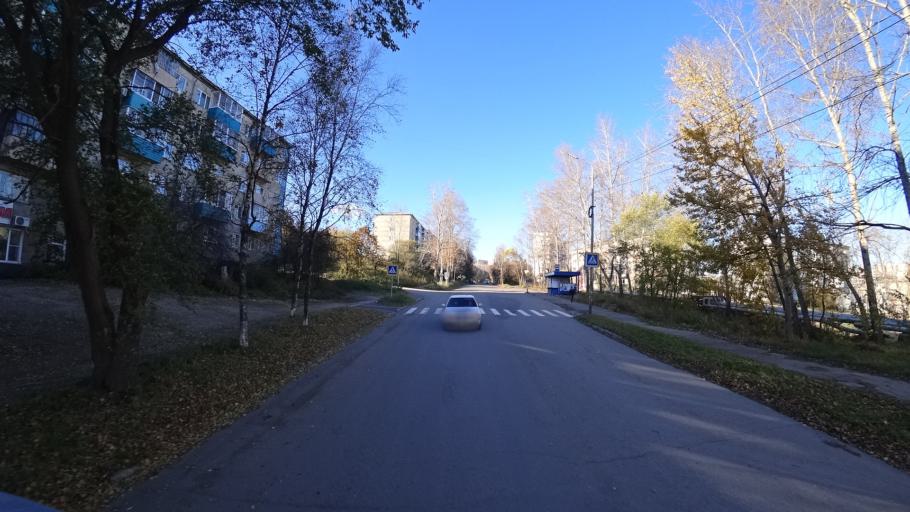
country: RU
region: Khabarovsk Krai
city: Amursk
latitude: 50.2358
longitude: 136.9054
